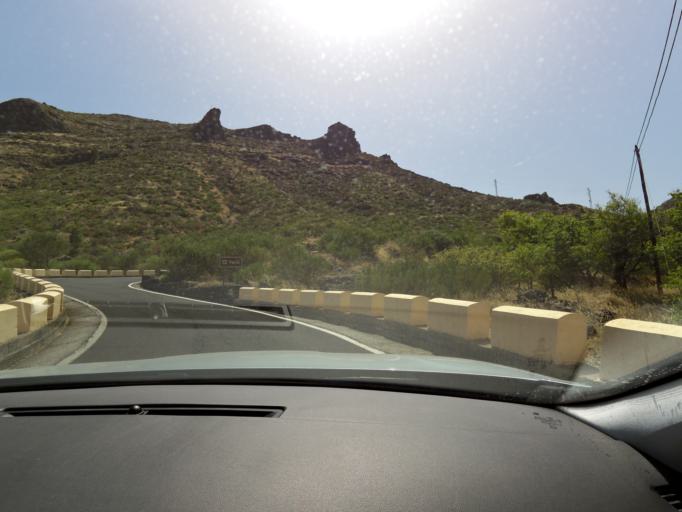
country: ES
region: Canary Islands
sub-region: Provincia de Santa Cruz de Tenerife
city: Santiago del Teide
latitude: 28.2971
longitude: -16.8181
